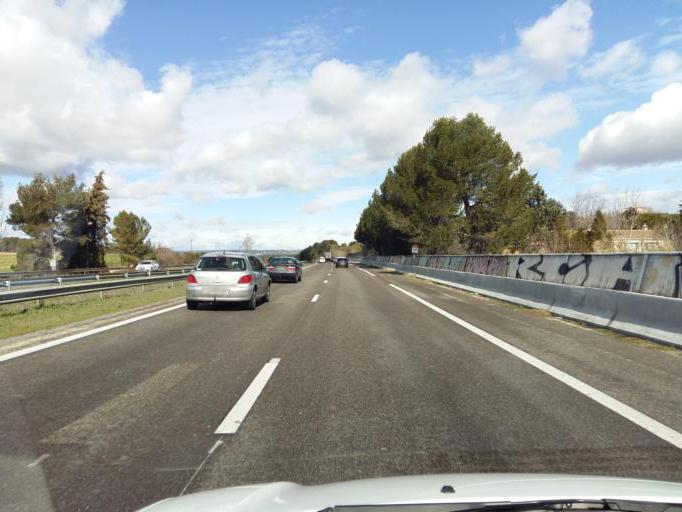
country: FR
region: Provence-Alpes-Cote d'Azur
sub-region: Departement des Bouches-du-Rhone
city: Bouc-Bel-Air
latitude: 43.4761
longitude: 5.4080
